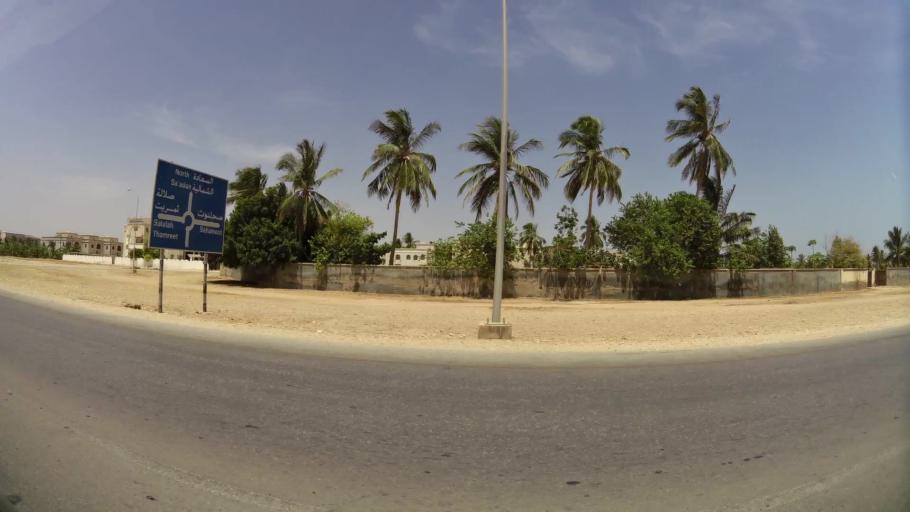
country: OM
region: Zufar
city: Salalah
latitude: 17.0650
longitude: 54.1498
